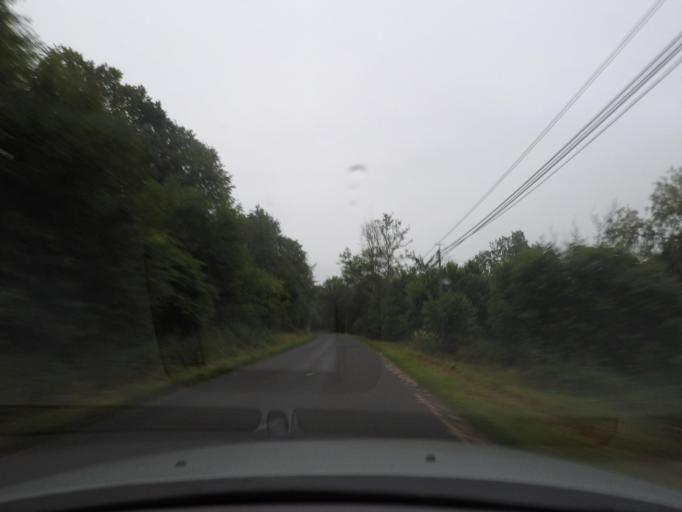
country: FR
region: Haute-Normandie
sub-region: Departement de la Seine-Maritime
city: Fontaine-le-Bourg
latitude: 49.5792
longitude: 1.2137
